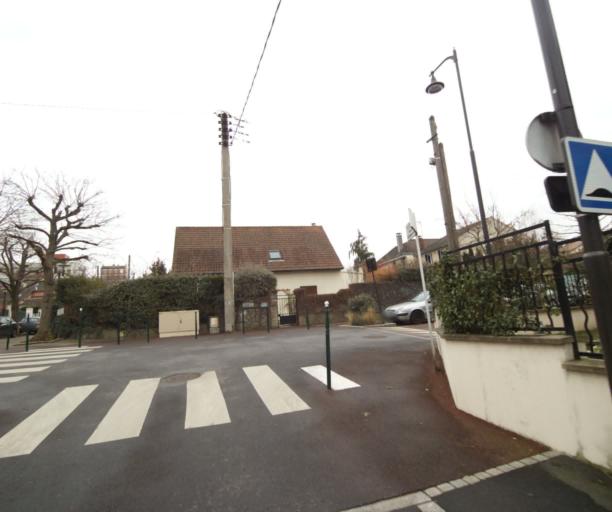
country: FR
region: Ile-de-France
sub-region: Departement des Hauts-de-Seine
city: Rueil-Malmaison
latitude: 48.8794
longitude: 2.1946
